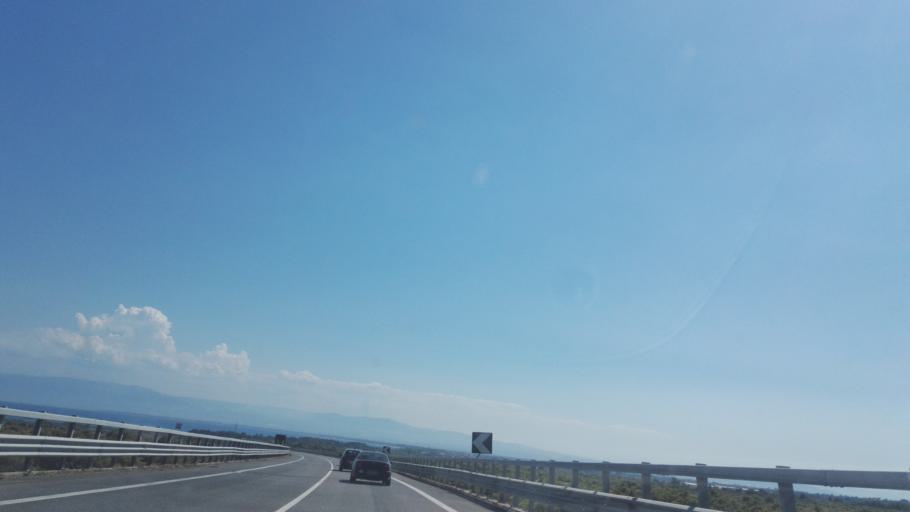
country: IT
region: Calabria
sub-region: Provincia di Cosenza
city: Trebisacce
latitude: 39.8559
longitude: 16.5089
